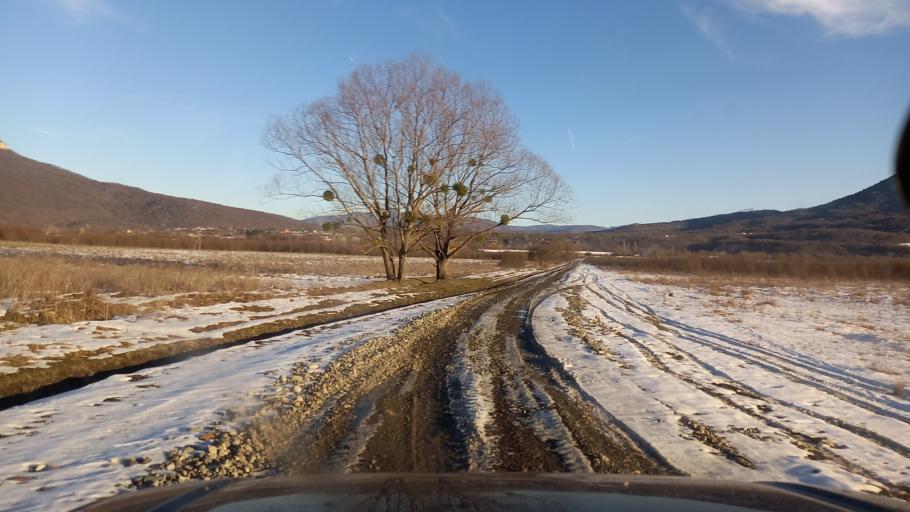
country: RU
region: Adygeya
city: Kamennomostskiy
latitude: 44.2289
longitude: 40.1723
